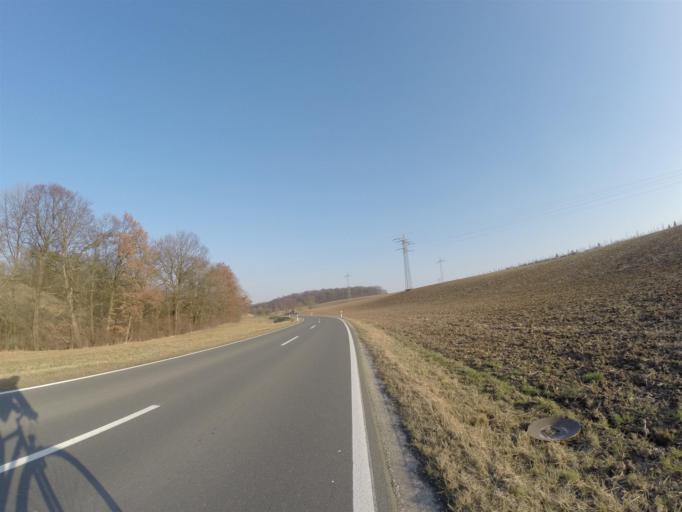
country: DE
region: Thuringia
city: Mellingen
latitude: 50.9407
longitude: 11.4089
